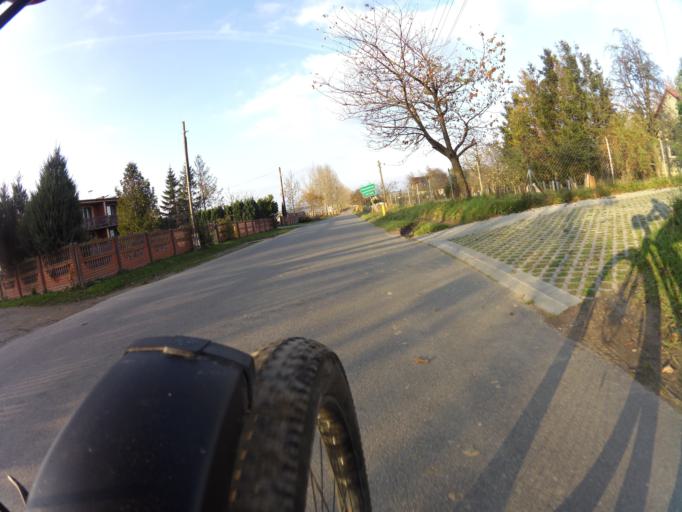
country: PL
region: Pomeranian Voivodeship
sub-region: Powiat pucki
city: Krokowa
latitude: 54.7680
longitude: 18.1798
